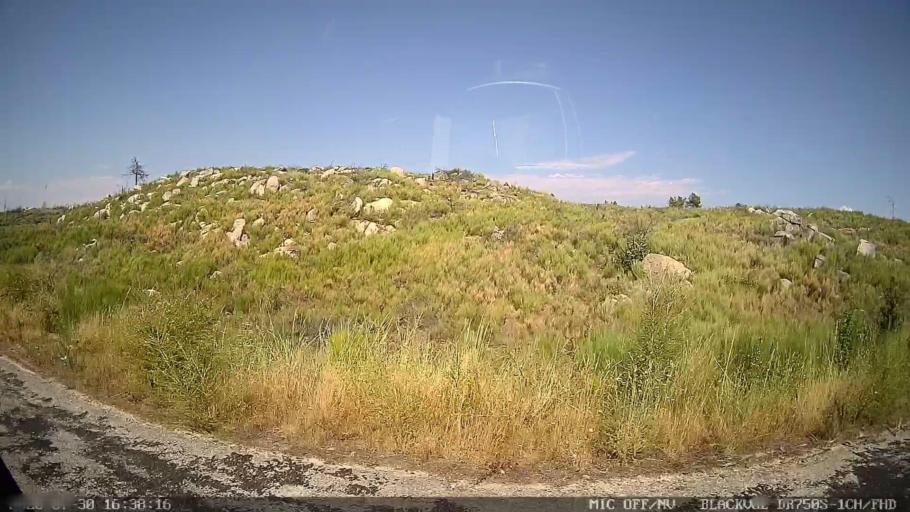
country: PT
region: Vila Real
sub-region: Sabrosa
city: Sabrosa
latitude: 41.3025
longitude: -7.4873
